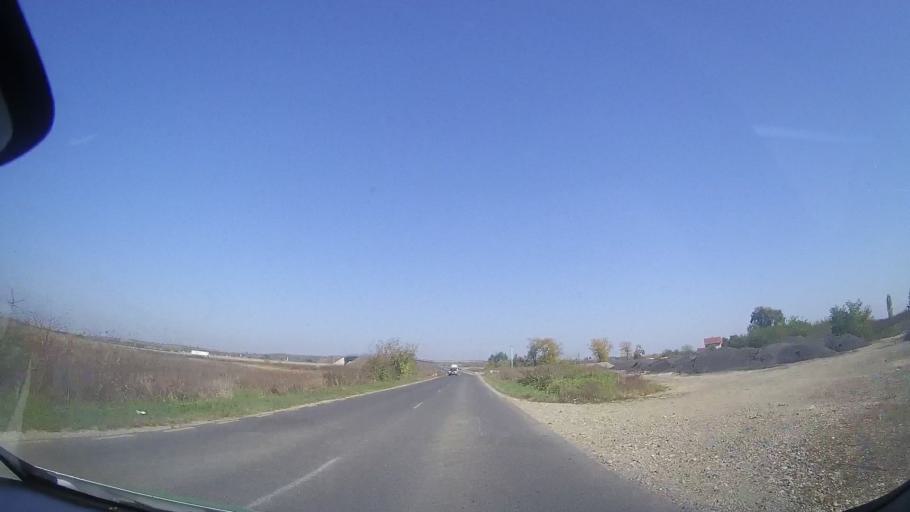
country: RO
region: Timis
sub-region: Comuna Balint
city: Balint
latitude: 45.7946
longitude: 21.8601
